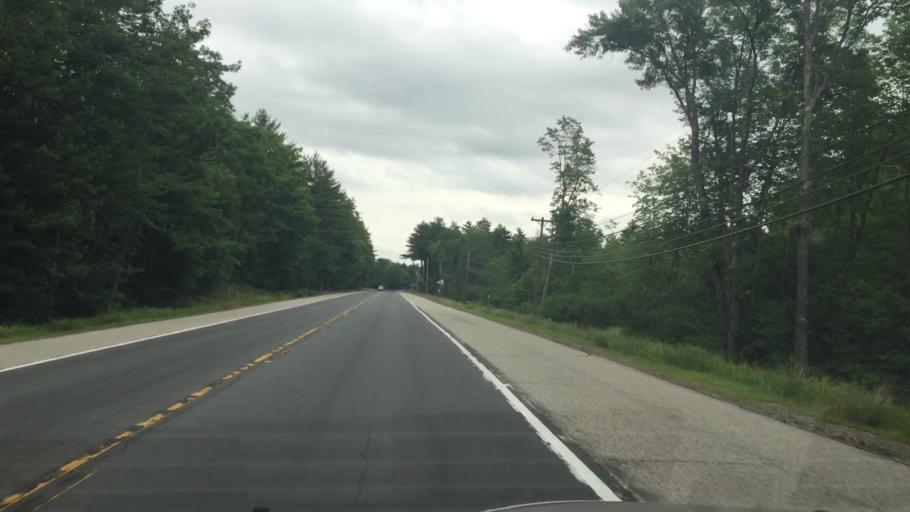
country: US
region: New Hampshire
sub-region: Carroll County
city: Tamworth
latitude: 43.8299
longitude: -71.2831
